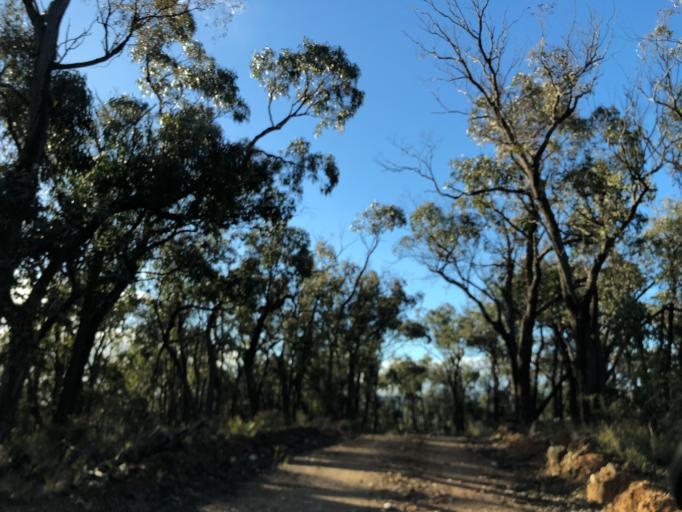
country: AU
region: Victoria
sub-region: Mount Alexander
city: Castlemaine
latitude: -37.2327
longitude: 144.2692
